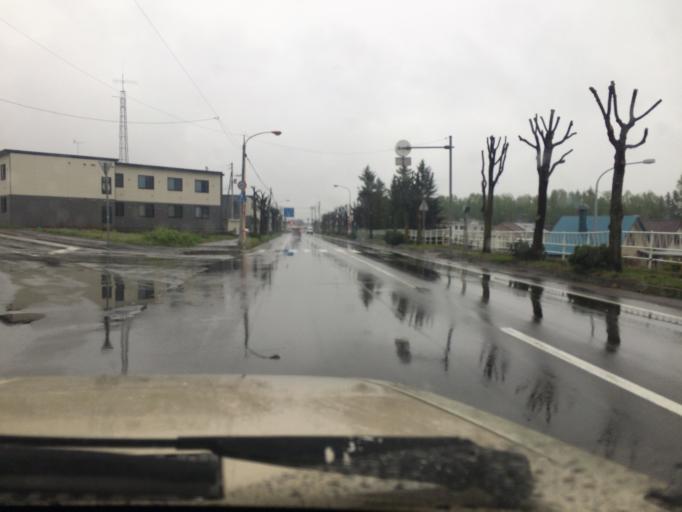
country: JP
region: Hokkaido
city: Obihiro
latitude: 42.9067
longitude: 143.0526
